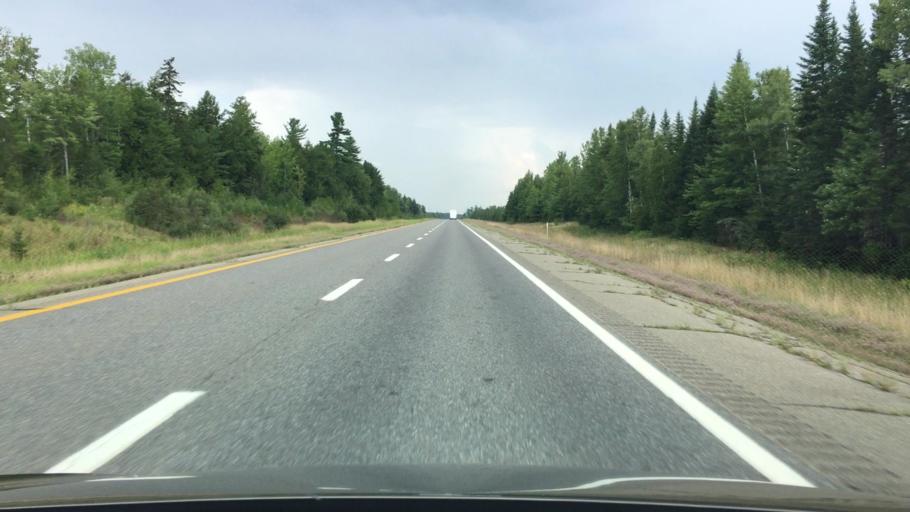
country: US
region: Maine
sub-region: Penobscot County
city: Medway
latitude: 45.5167
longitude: -68.5524
